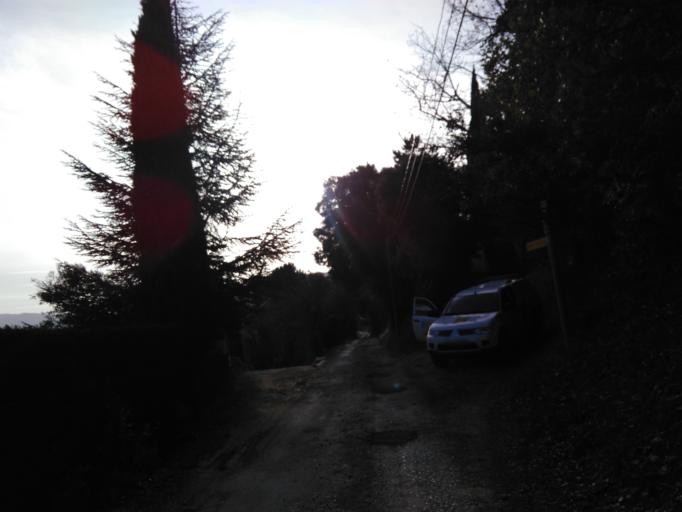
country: FR
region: Provence-Alpes-Cote d'Azur
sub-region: Departement du Vaucluse
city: Vaison-la-Romaine
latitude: 44.2118
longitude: 5.0858
